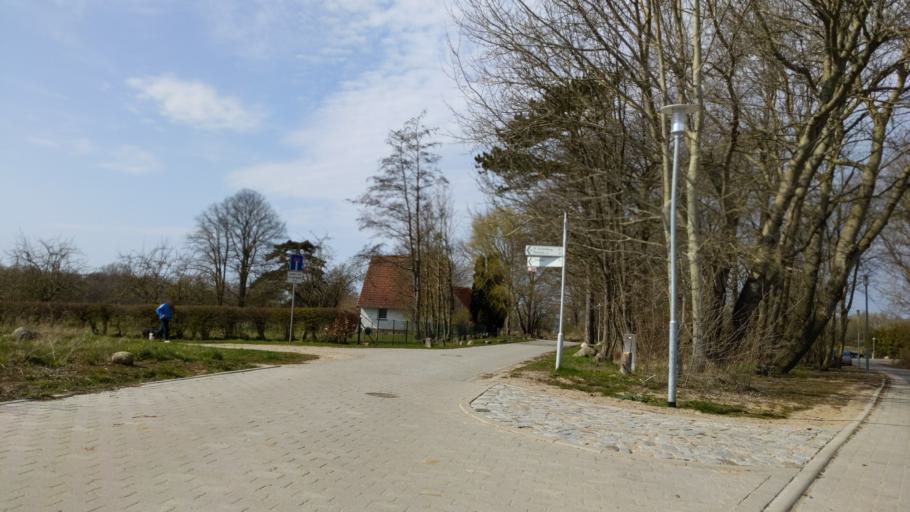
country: DE
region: Mecklenburg-Vorpommern
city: Dassow
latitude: 53.9624
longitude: 10.9389
